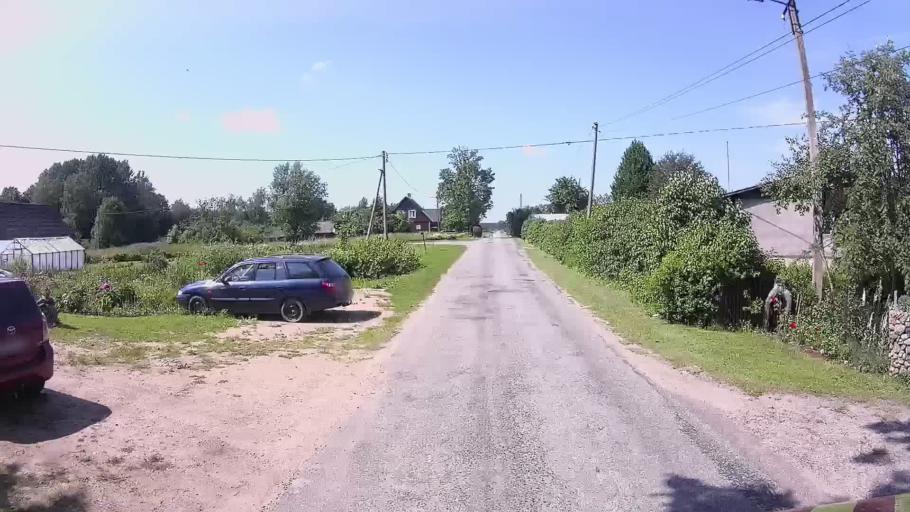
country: EE
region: Viljandimaa
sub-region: Karksi vald
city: Karksi-Nuia
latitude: 57.9940
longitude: 25.5365
